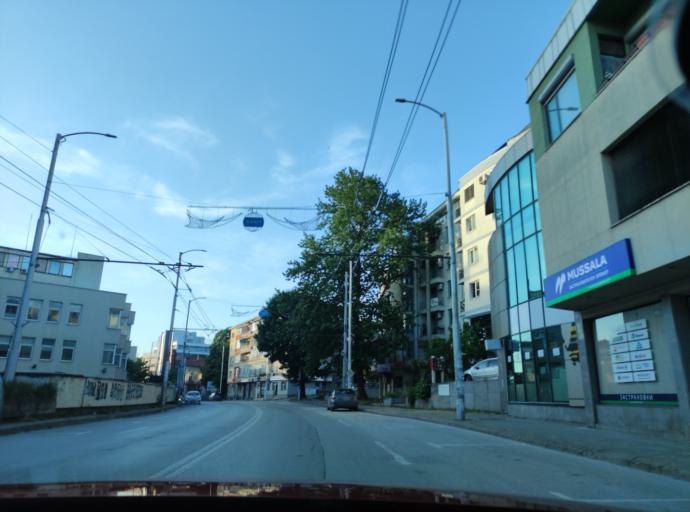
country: BG
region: Pleven
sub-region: Obshtina Pleven
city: Pleven
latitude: 43.4060
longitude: 24.6212
